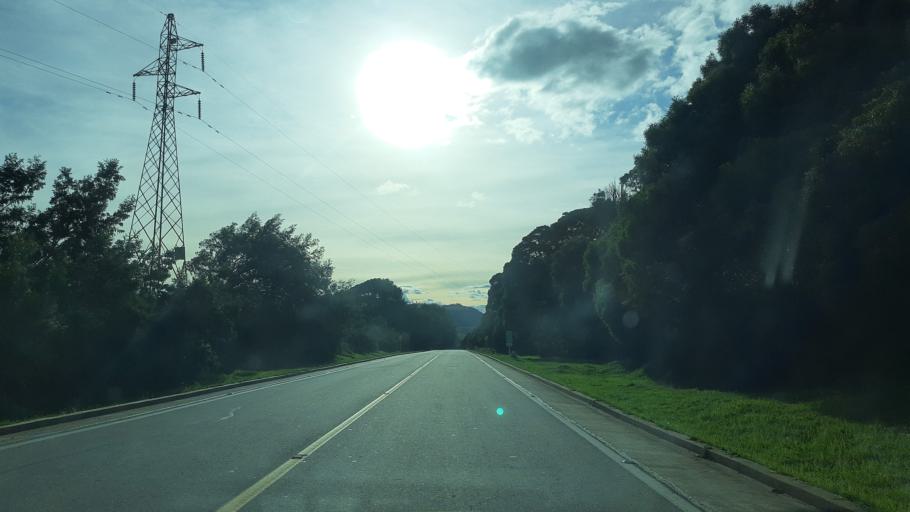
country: CO
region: Cundinamarca
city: Choconta
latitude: 5.0979
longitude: -73.6931
